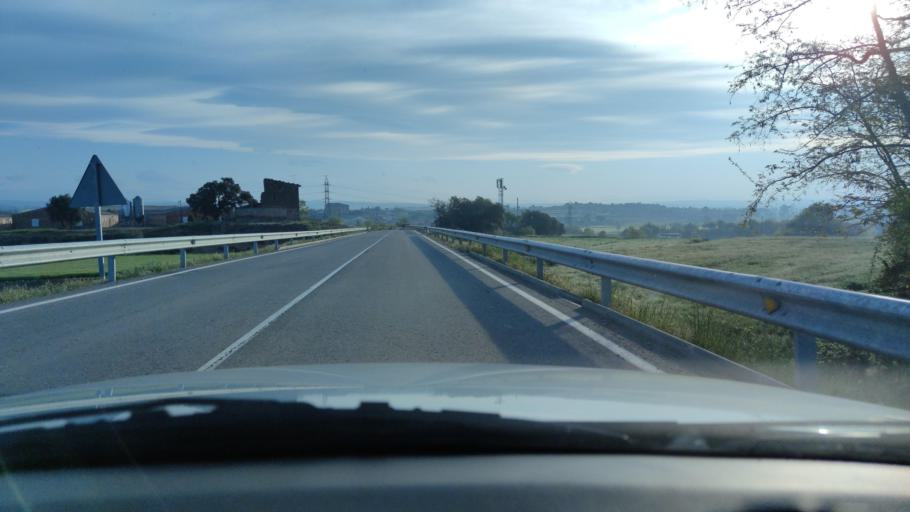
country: ES
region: Catalonia
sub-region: Provincia de Lleida
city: Agramunt
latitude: 41.7888
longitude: 1.0446
